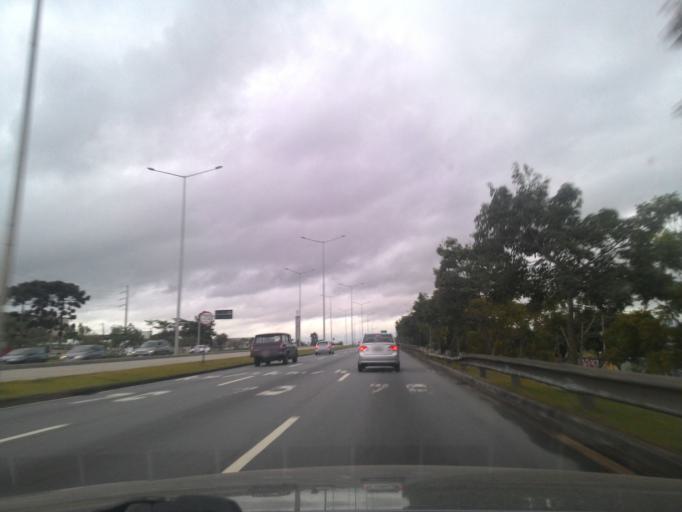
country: BR
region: Parana
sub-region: Curitiba
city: Curitiba
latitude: -25.4905
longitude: -49.2709
